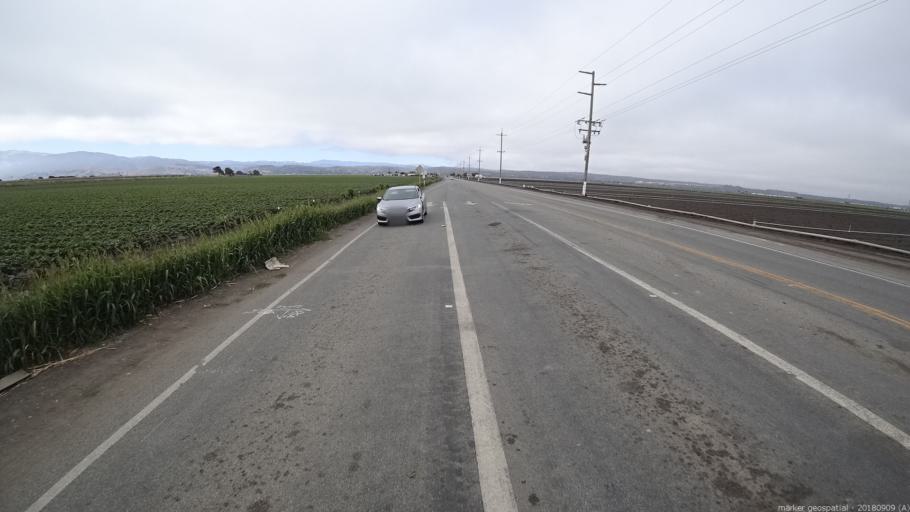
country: US
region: California
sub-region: Monterey County
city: Salinas
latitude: 36.6665
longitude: -121.6853
